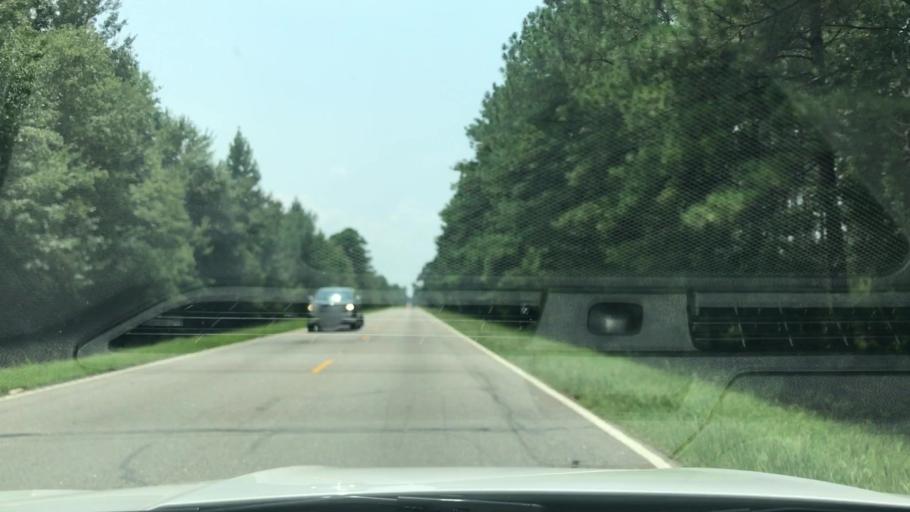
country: US
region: South Carolina
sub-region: Georgetown County
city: Georgetown
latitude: 33.5419
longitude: -79.2283
